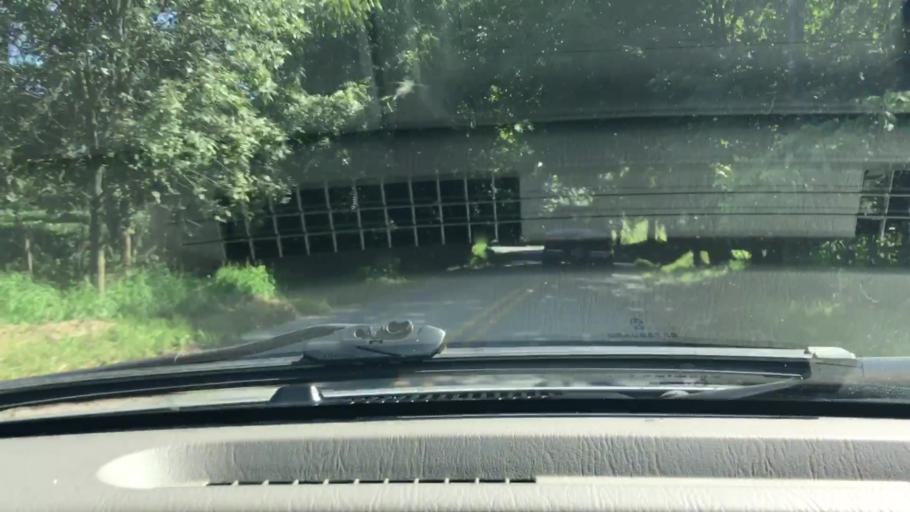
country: US
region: Pennsylvania
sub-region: Lancaster County
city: Elizabethtown
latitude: 40.1833
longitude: -76.6119
